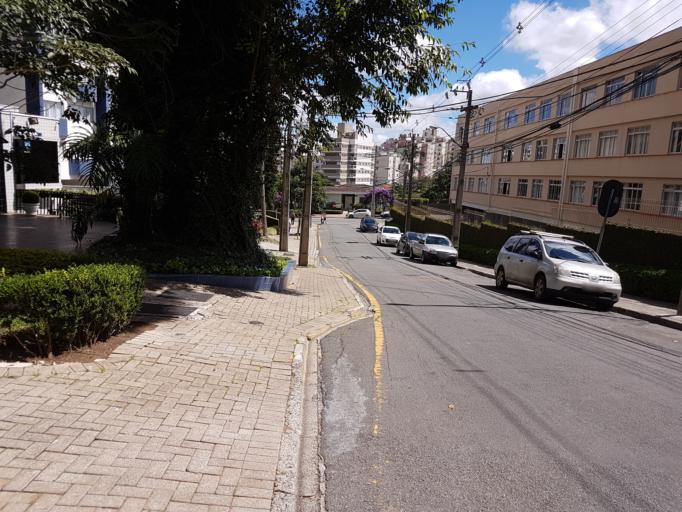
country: BR
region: Parana
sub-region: Curitiba
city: Curitiba
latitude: -25.4358
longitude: -49.2416
